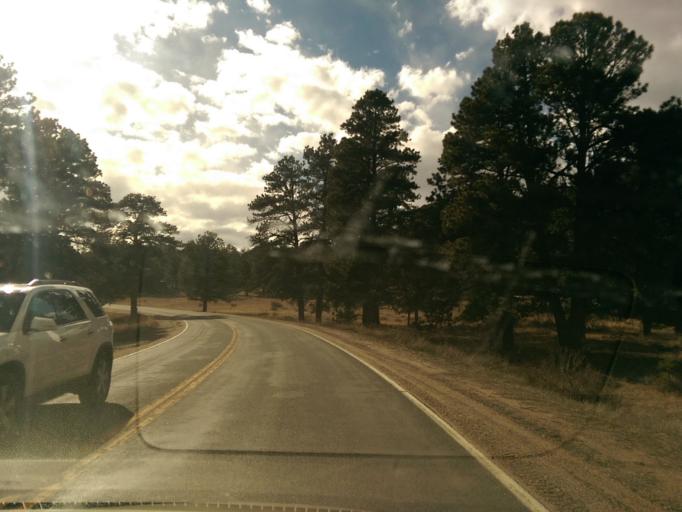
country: US
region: Colorado
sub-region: Larimer County
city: Estes Park
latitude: 40.3695
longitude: -105.5683
